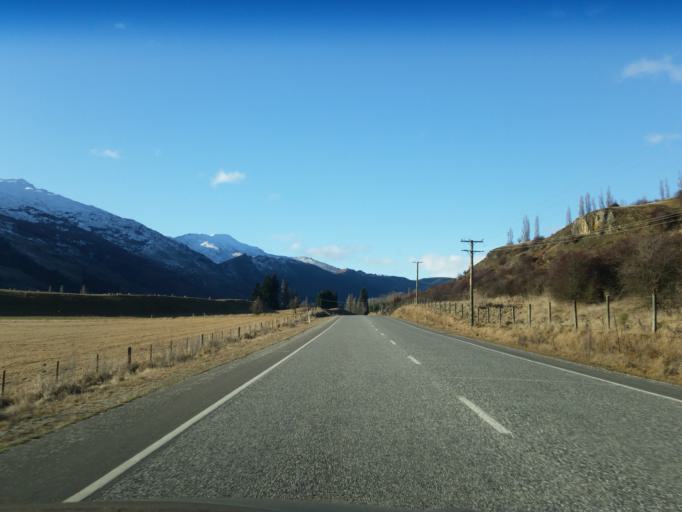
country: NZ
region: Otago
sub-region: Queenstown-Lakes District
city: Queenstown
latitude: -44.9641
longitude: 168.7155
